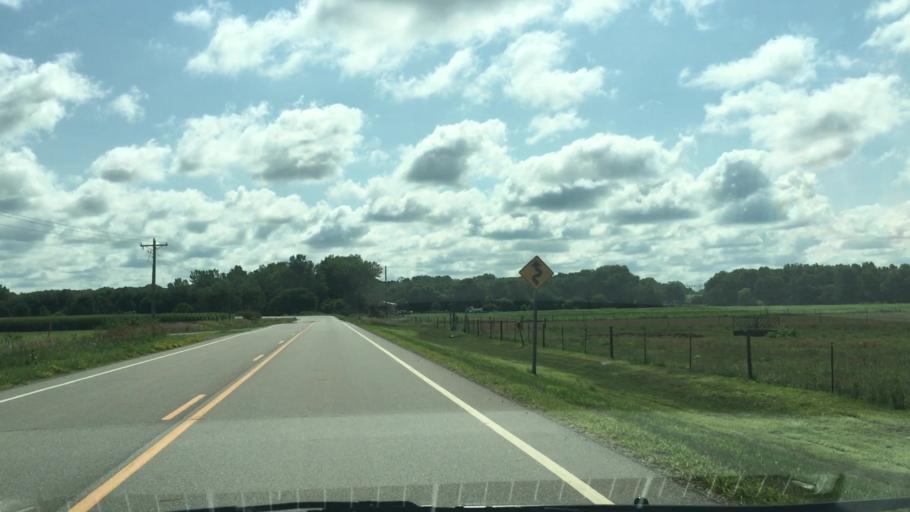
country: US
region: Iowa
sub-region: Linn County
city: Lisbon
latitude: 41.8409
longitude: -91.4017
